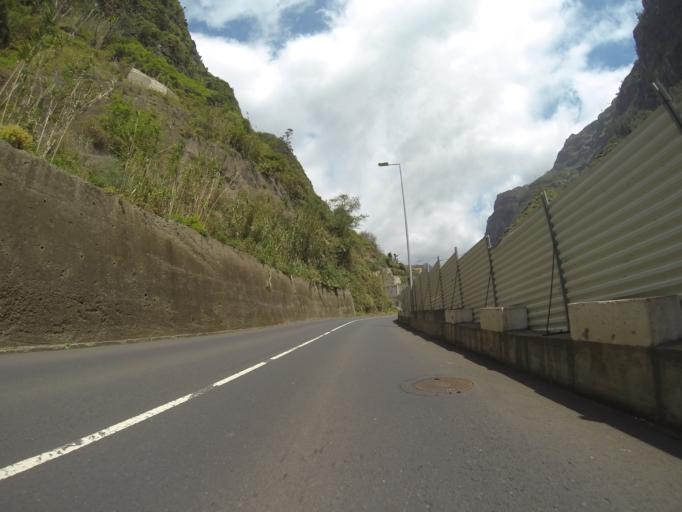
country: PT
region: Madeira
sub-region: Ribeira Brava
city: Campanario
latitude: 32.7085
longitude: -17.0371
